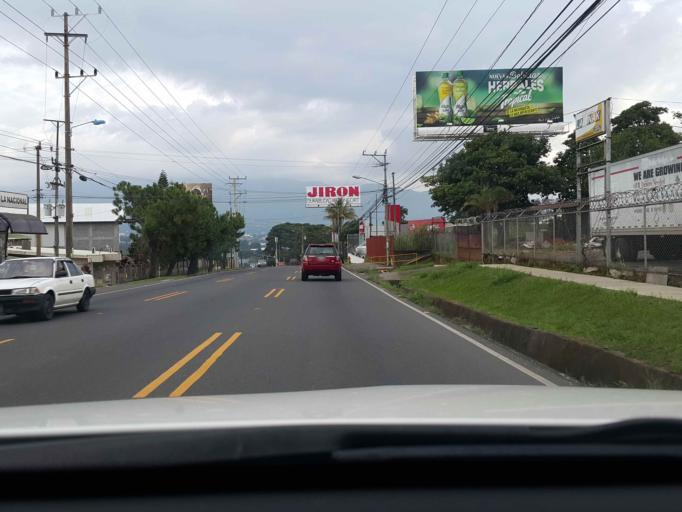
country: CR
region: Heredia
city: San Pablo
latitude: 9.9799
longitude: -84.1104
